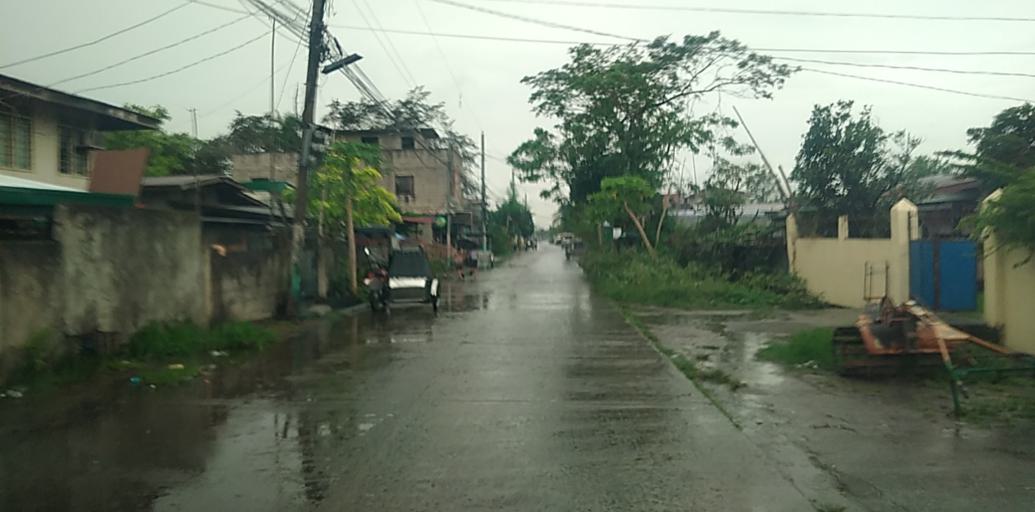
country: PH
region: Central Luzon
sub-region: Province of Pampanga
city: Arenas
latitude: 15.1646
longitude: 120.6898
